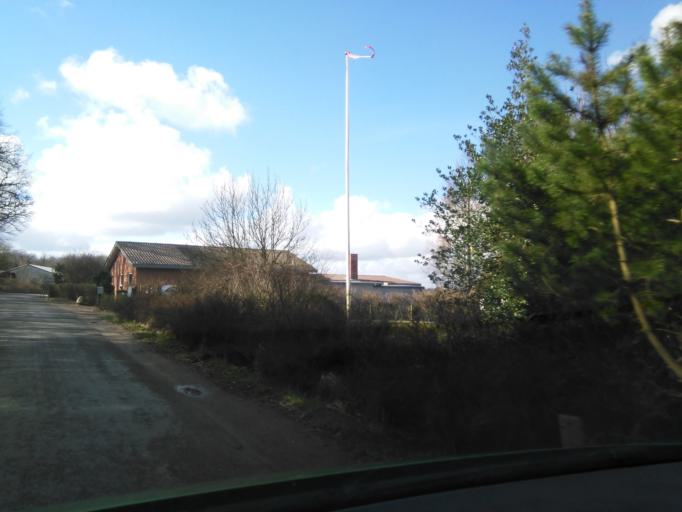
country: DK
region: Central Jutland
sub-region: Arhus Kommune
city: Beder
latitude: 56.0459
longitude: 10.2156
